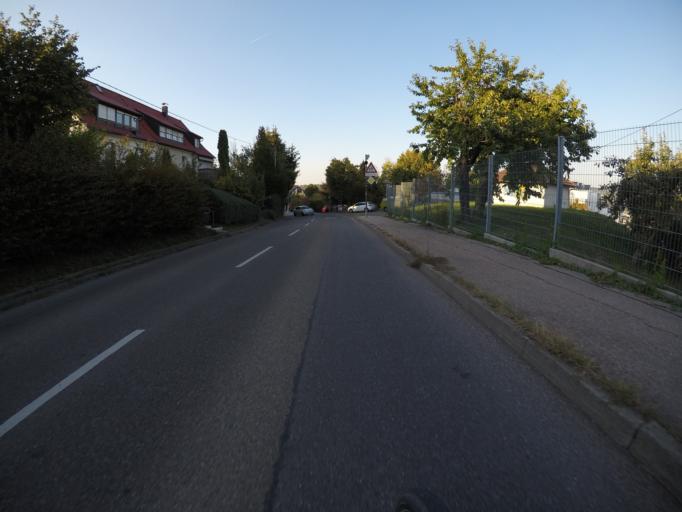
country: DE
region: Baden-Wuerttemberg
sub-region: Regierungsbezirk Stuttgart
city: Ostfildern
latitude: 48.7485
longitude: 9.2410
